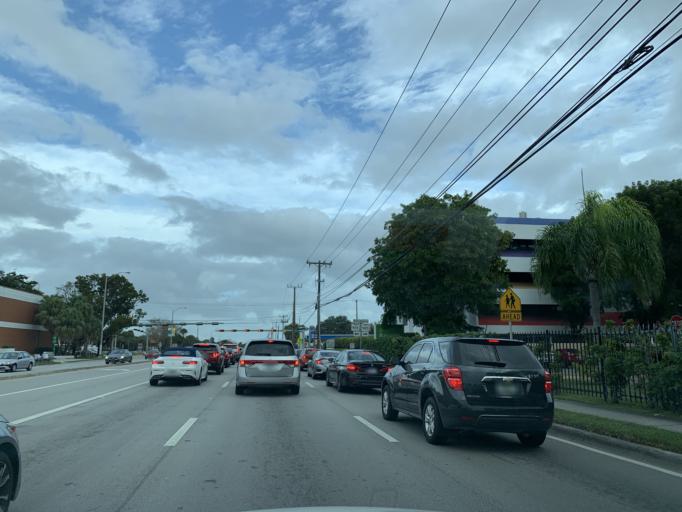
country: US
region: Florida
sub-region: Miami-Dade County
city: Sunset
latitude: 25.6869
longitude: -80.3671
